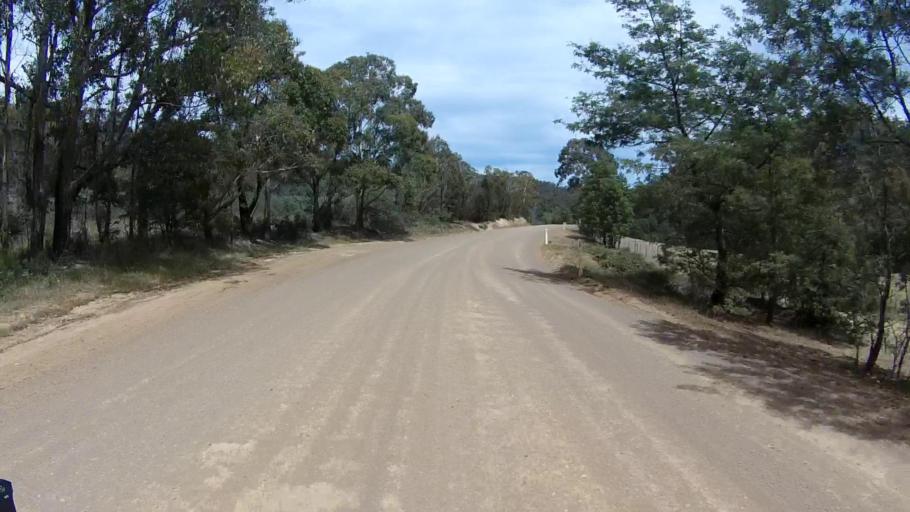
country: AU
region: Tasmania
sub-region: Sorell
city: Sorell
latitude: -42.8002
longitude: 147.6626
